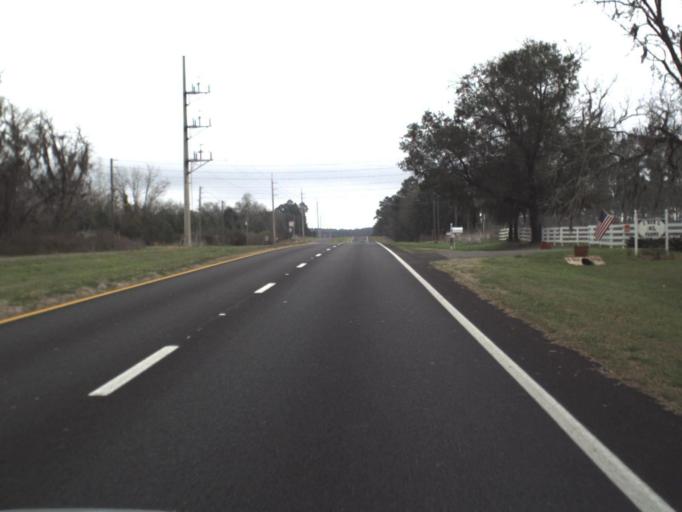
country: US
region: Florida
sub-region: Jefferson County
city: Monticello
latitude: 30.4117
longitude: -83.9396
